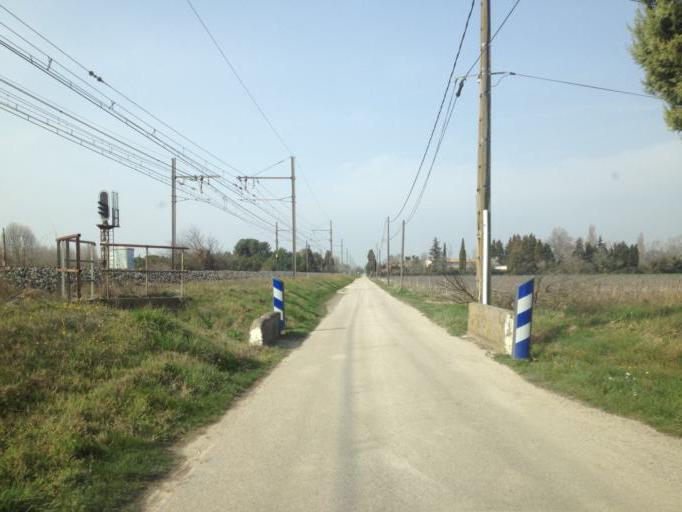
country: FR
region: Provence-Alpes-Cote d'Azur
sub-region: Departement du Vaucluse
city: Courthezon
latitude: 44.0760
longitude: 4.8906
